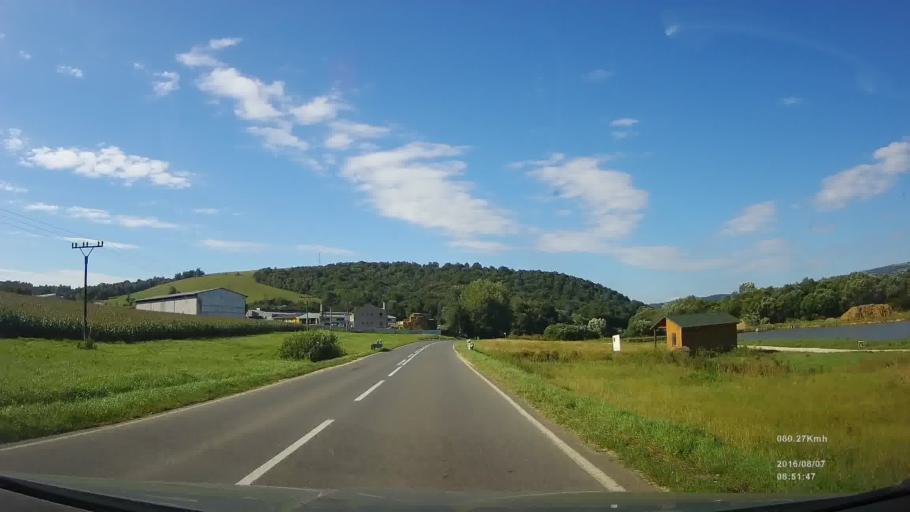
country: SK
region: Presovsky
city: Stropkov
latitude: 49.2329
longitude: 21.6734
